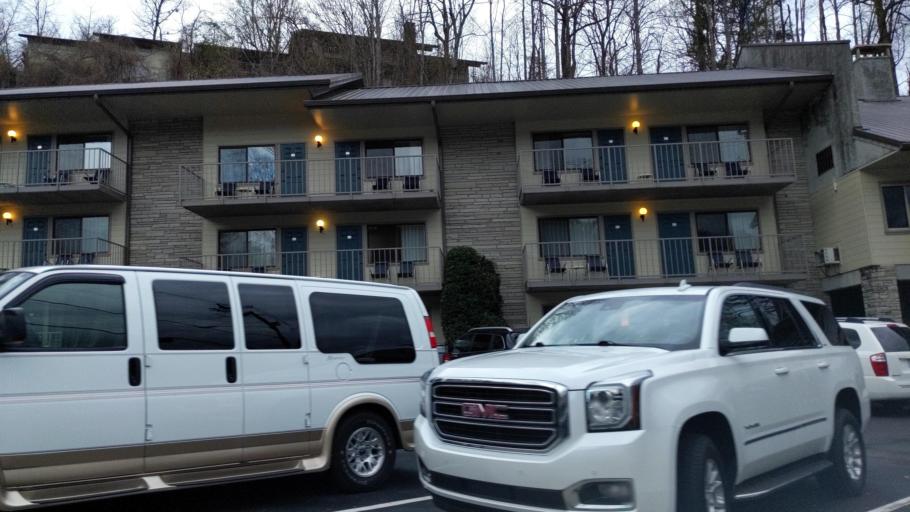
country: US
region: Tennessee
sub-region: Sevier County
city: Gatlinburg
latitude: 35.7111
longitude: -83.5138
